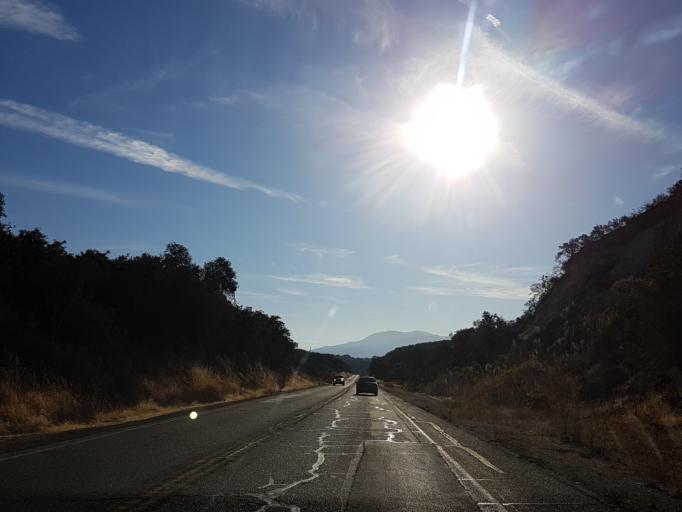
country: US
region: California
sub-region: Santa Barbara County
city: Santa Ynez
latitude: 34.5637
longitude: -119.9341
